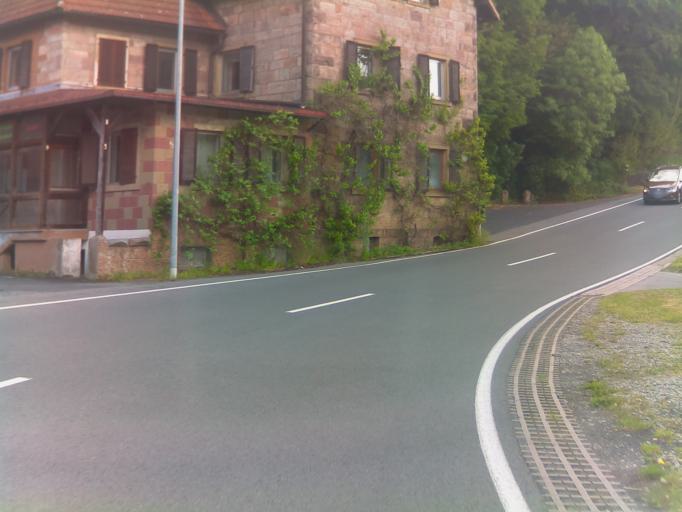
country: DE
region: Bavaria
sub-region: Regierungsbezirk Unterfranken
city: Sandberg
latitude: 50.3380
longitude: 9.9897
